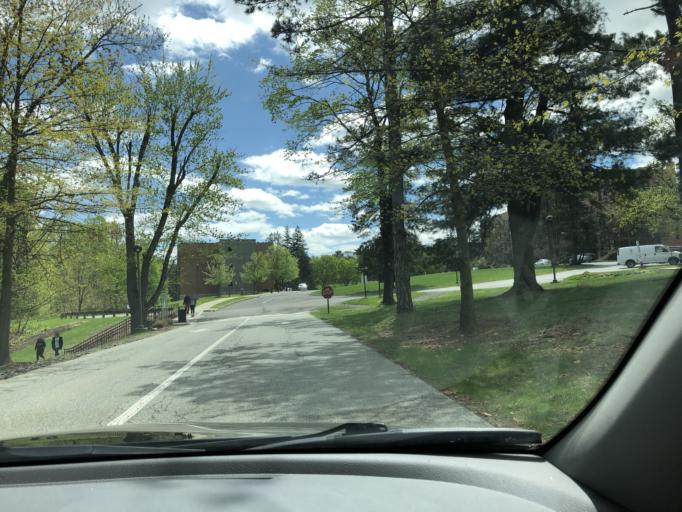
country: US
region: New Jersey
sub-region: Essex County
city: Caldwell
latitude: 40.8357
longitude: -74.2730
